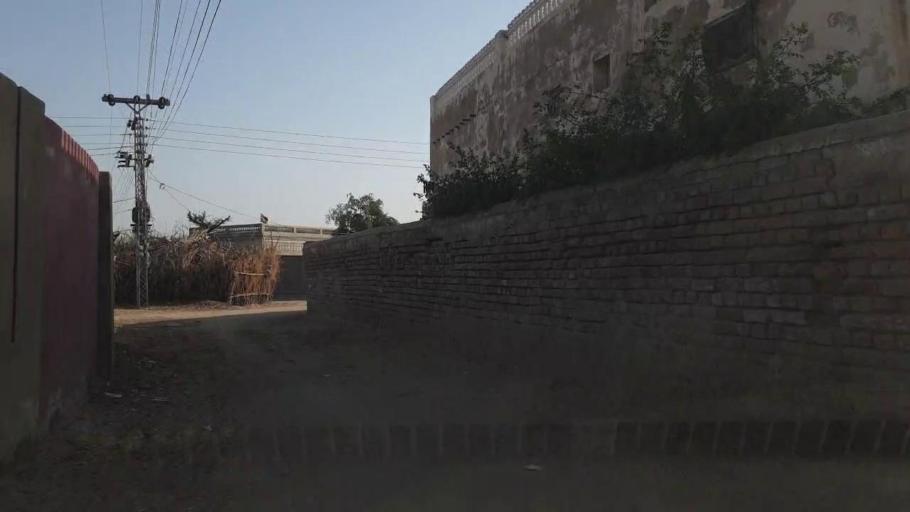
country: PK
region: Sindh
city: Dhoro Naro
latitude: 25.4656
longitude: 69.5746
